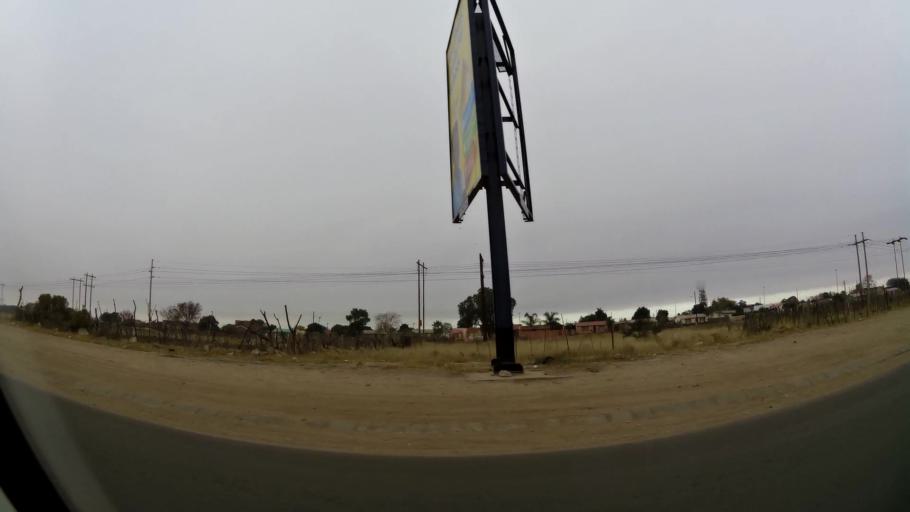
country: ZA
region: Limpopo
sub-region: Capricorn District Municipality
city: Polokwane
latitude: -23.8380
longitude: 29.3971
